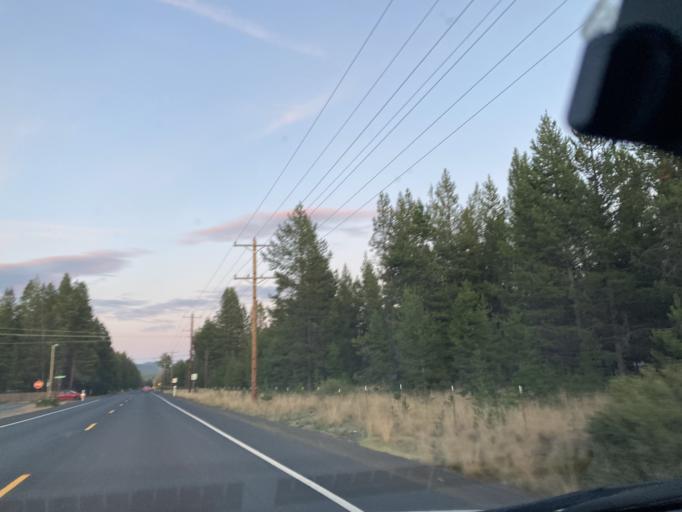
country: US
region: Oregon
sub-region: Deschutes County
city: Three Rivers
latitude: 43.8194
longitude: -121.4636
